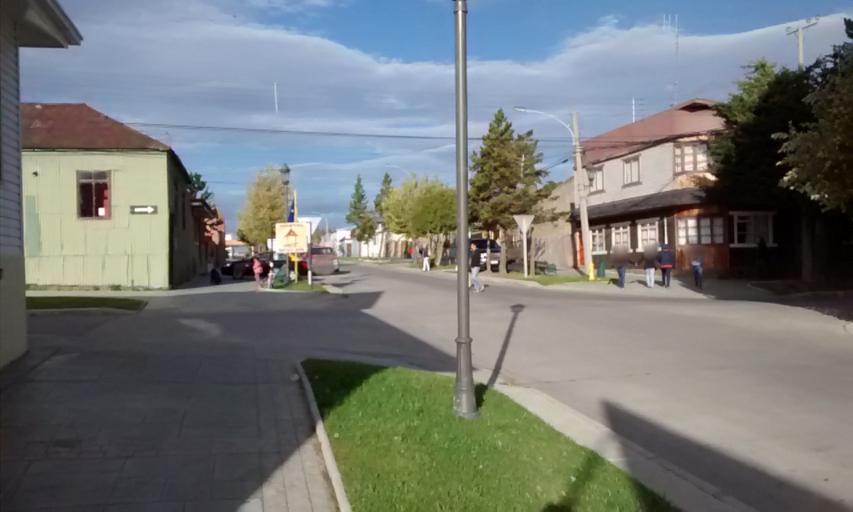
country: CL
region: Magallanes
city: Puerto Natales
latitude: -51.7264
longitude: -72.5109
